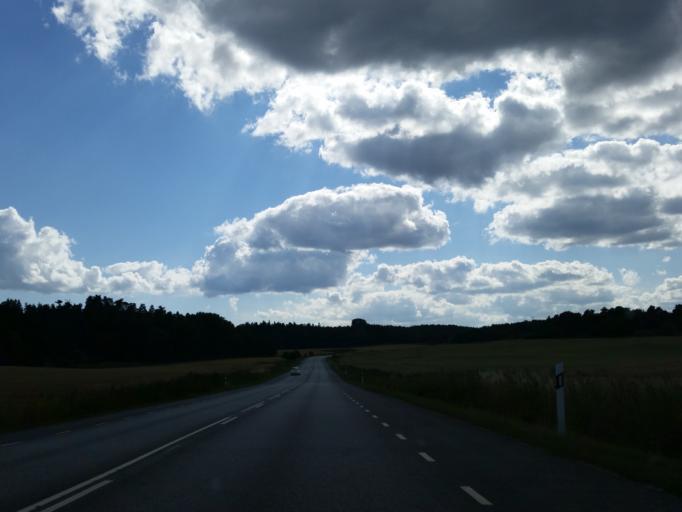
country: SE
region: Soedermanland
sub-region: Trosa Kommun
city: Vagnharad
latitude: 58.9535
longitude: 17.5513
